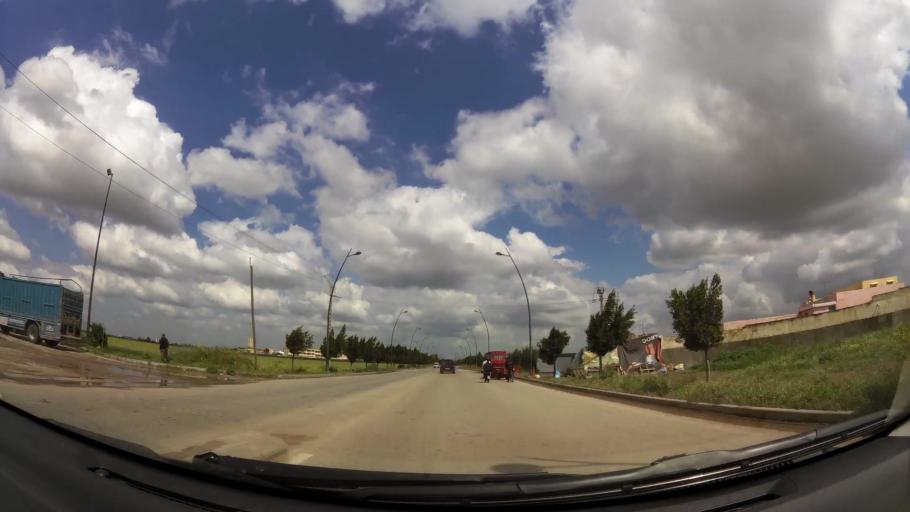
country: MA
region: Chaouia-Ouardigha
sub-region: Settat Province
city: Berrechid
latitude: 33.2609
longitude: -7.6125
